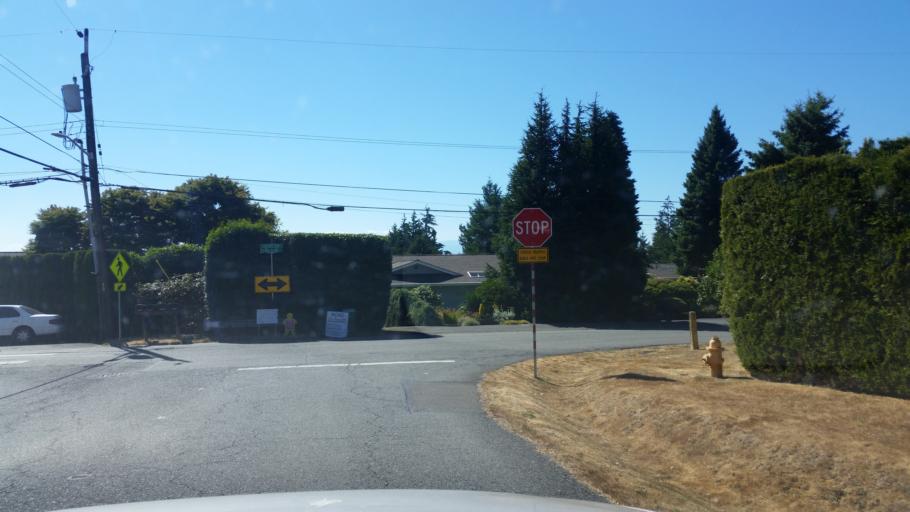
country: US
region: Washington
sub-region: Snohomish County
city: Esperance
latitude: 47.7742
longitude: -122.3683
